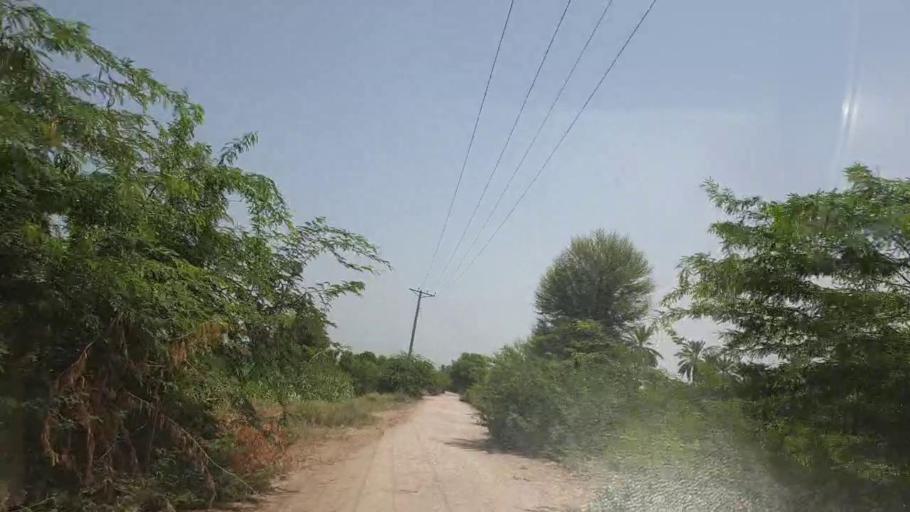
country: PK
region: Sindh
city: Kot Diji
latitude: 27.2825
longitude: 68.6388
